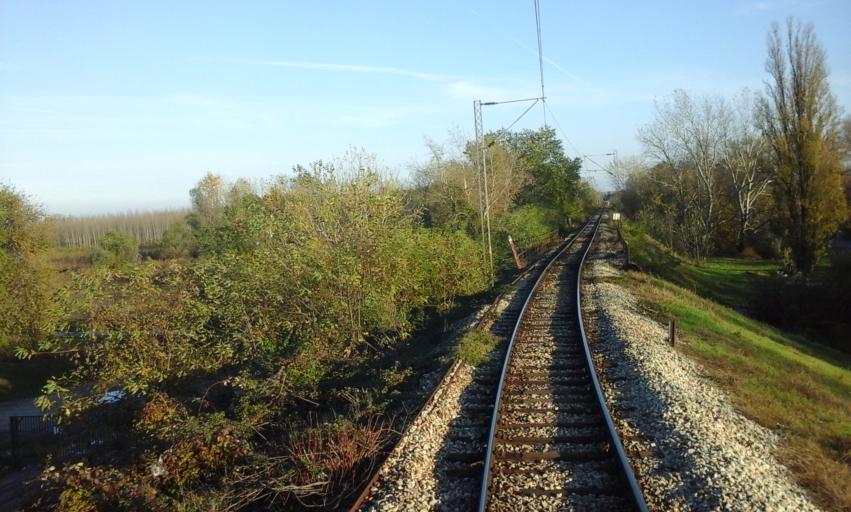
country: RS
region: Autonomna Pokrajina Vojvodina
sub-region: Juznobacki Okrug
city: Petrovaradin
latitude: 45.2596
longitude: 19.8649
